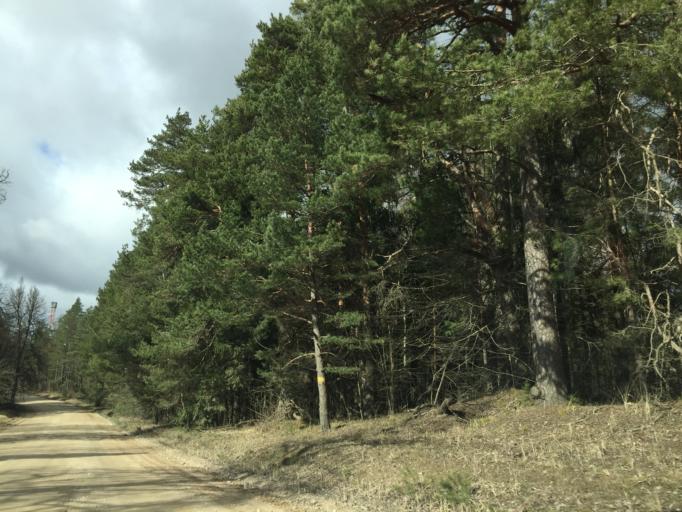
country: LV
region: Akniste
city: Akniste
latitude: 56.1102
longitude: 25.9160
